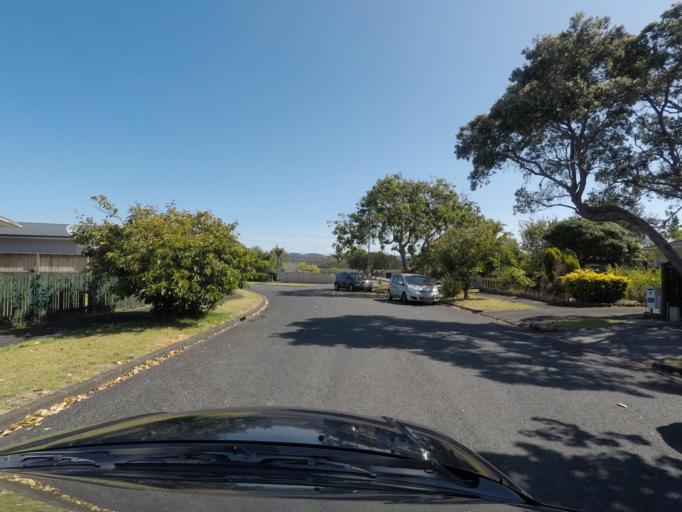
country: NZ
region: Auckland
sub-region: Auckland
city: Rosebank
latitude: -36.8902
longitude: 174.6764
